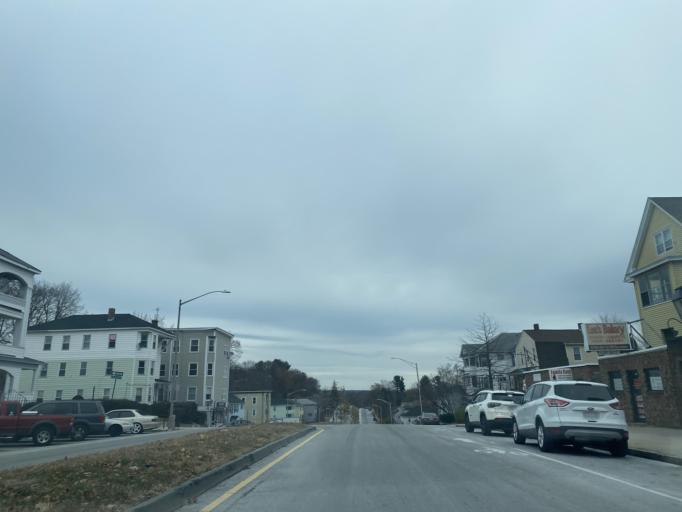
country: US
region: Massachusetts
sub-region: Worcester County
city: Hamilton
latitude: 42.2561
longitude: -71.7801
